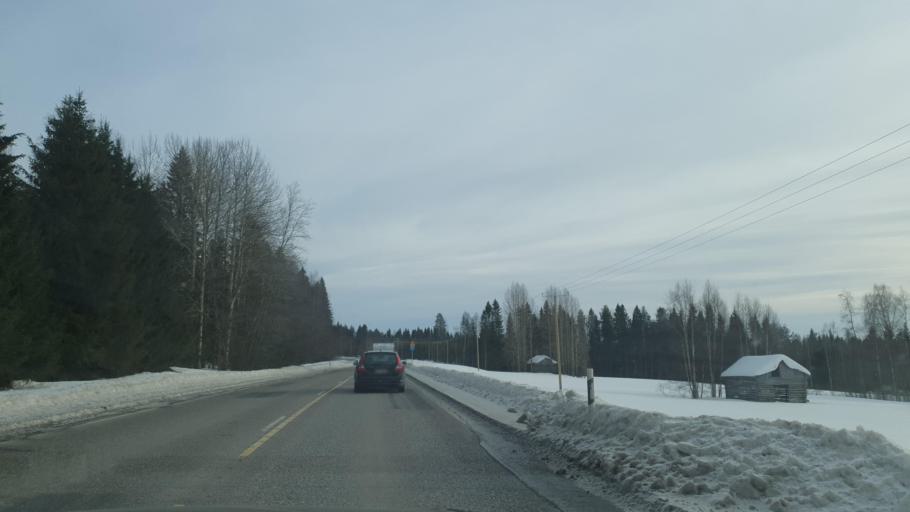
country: FI
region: Kainuu
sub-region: Kajaani
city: Kajaani
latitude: 64.4293
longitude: 27.5802
